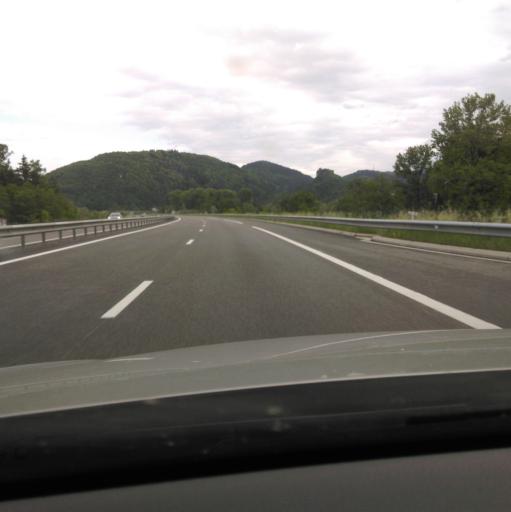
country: FR
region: Rhone-Alpes
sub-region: Departement de l'Ain
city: Montreal-la-Cluse
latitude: 46.1697
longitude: 5.5607
